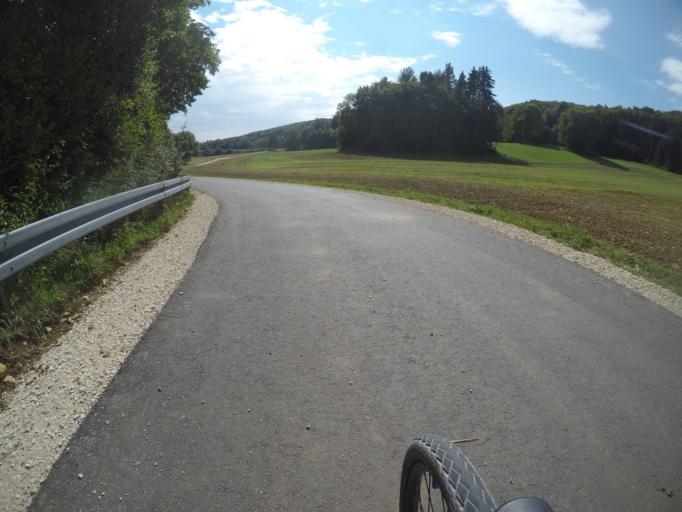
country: DE
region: Baden-Wuerttemberg
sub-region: Tuebingen Region
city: Munsingen
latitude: 48.3792
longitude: 9.5141
